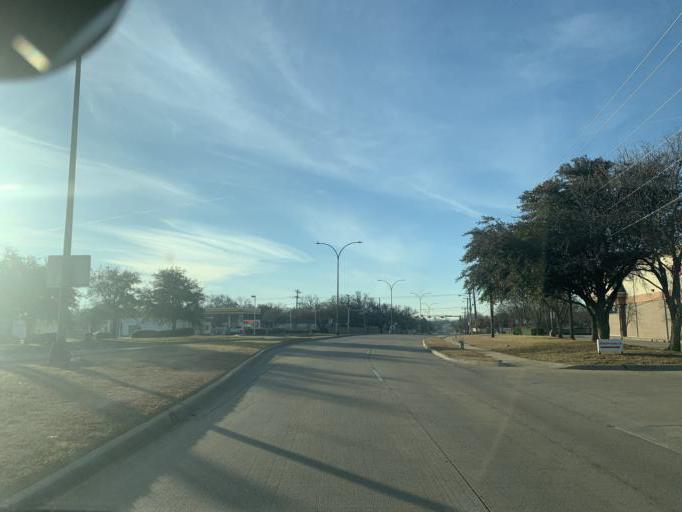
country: US
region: Texas
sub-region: Tarrant County
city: Arlington
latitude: 32.7758
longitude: -97.0738
